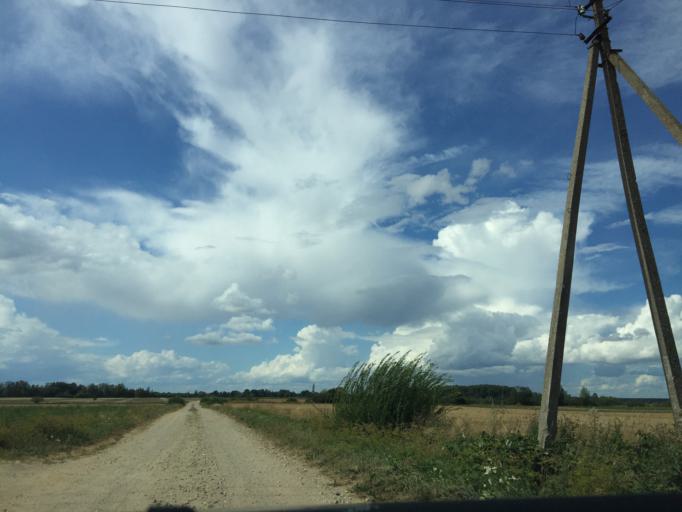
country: LT
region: Siauliu apskritis
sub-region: Joniskis
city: Joniskis
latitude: 56.3151
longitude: 23.6339
